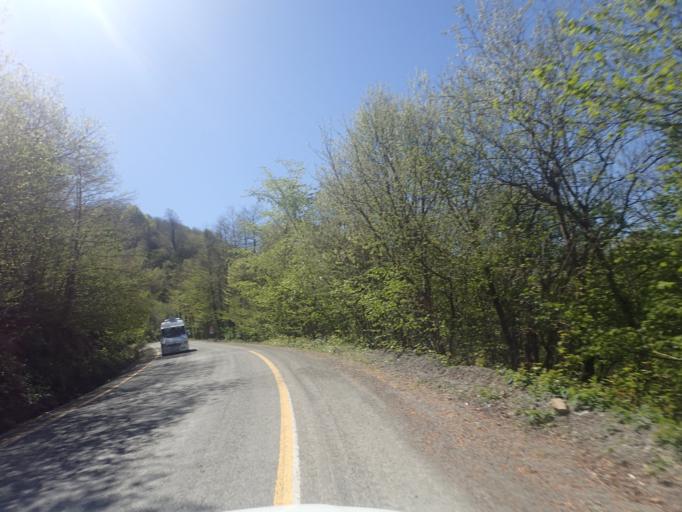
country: TR
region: Ordu
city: Kabaduz
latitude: 40.8129
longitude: 37.9072
